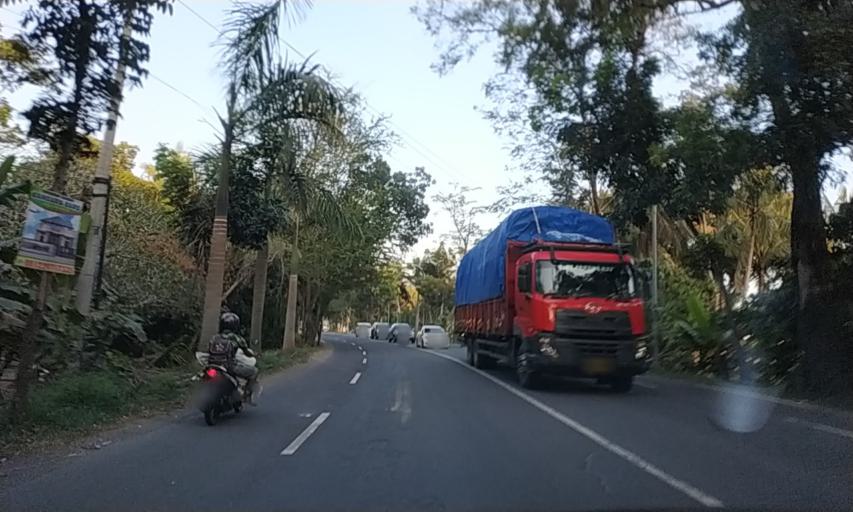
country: ID
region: Daerah Istimewa Yogyakarta
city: Srandakan
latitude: -7.8856
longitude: 110.0509
